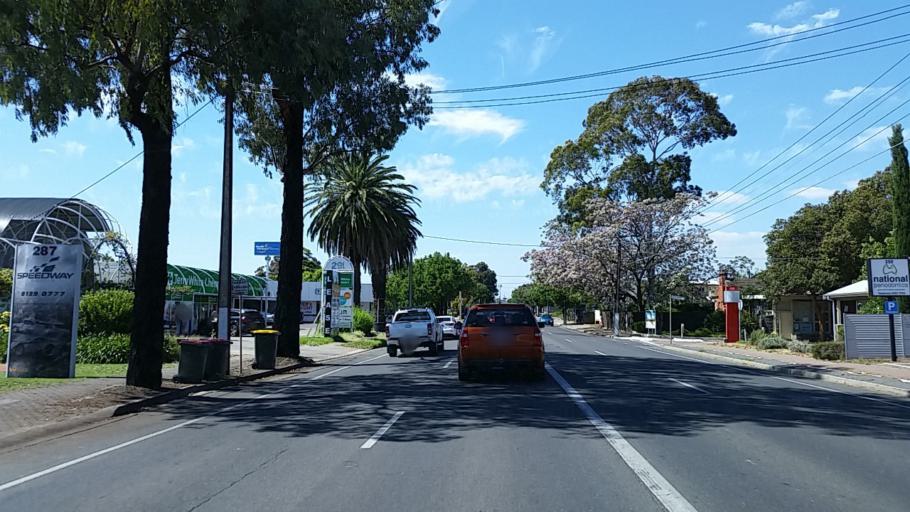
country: AU
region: South Australia
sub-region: Norwood Payneham St Peters
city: Royston Park
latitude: -34.9014
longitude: 138.6348
